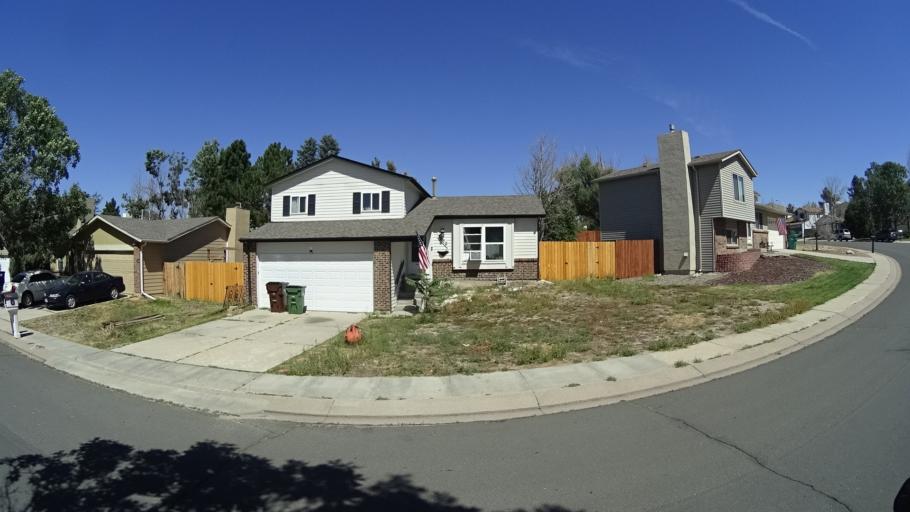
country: US
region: Colorado
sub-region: El Paso County
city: Black Forest
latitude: 38.9414
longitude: -104.7577
